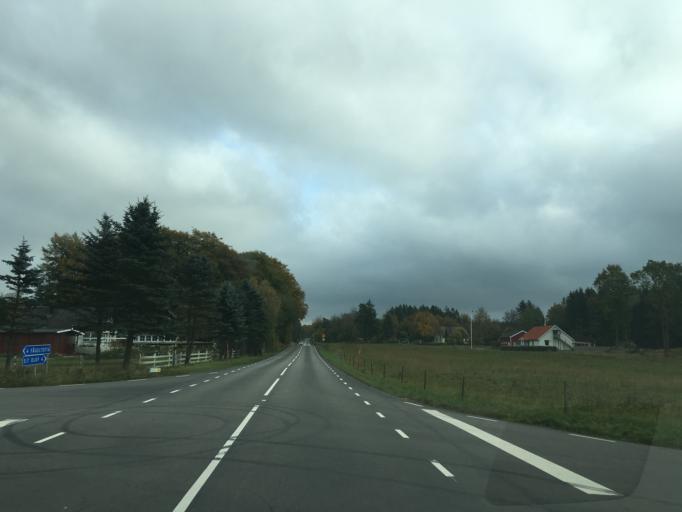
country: SE
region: Skane
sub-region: Tomelilla Kommun
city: Tomelilla
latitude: 55.6376
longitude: 14.0746
